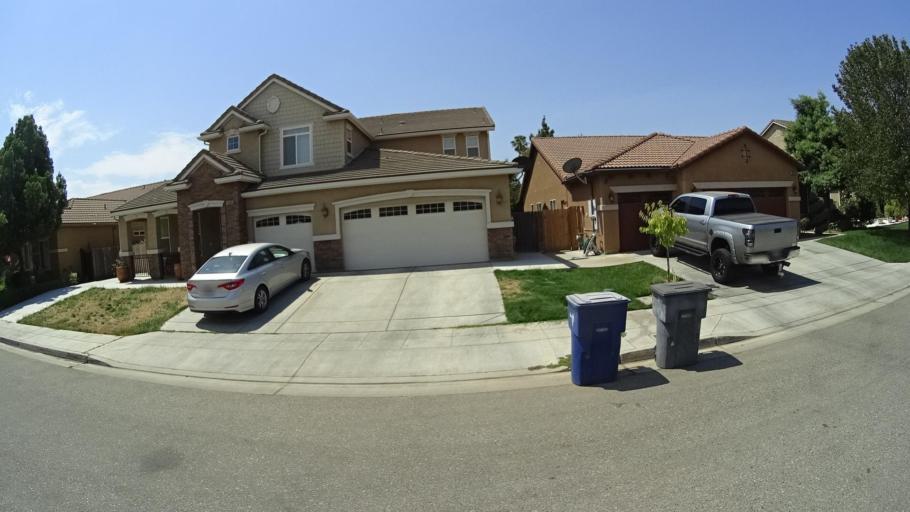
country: US
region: California
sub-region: Fresno County
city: Sunnyside
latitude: 36.7372
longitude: -119.6880
